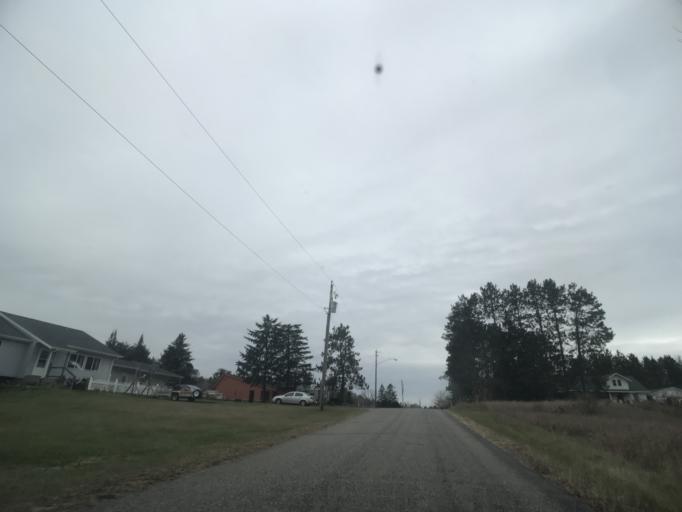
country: US
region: Wisconsin
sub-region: Menominee County
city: Legend Lake
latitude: 45.1821
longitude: -88.4697
